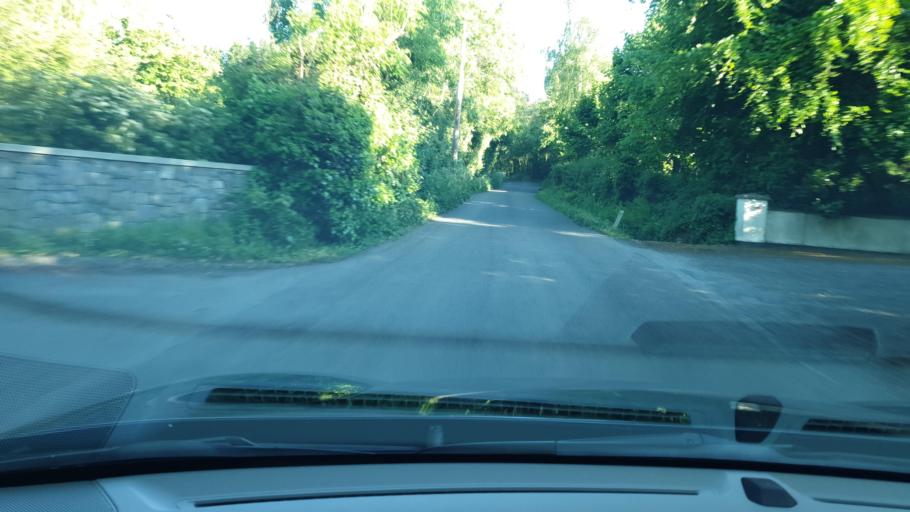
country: IE
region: Leinster
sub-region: Fingal County
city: Swords
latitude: 53.4945
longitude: -6.2299
